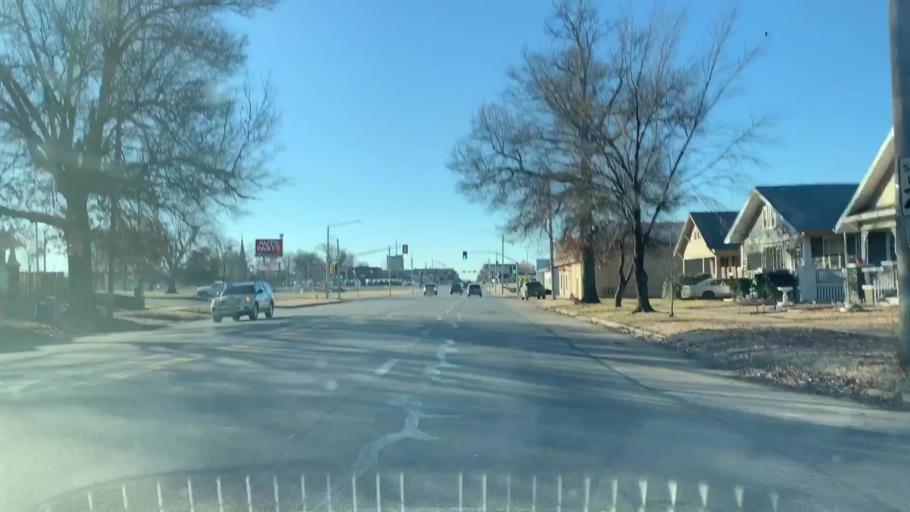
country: US
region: Kansas
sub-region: Crawford County
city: Pittsburg
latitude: 37.4211
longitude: -94.7050
